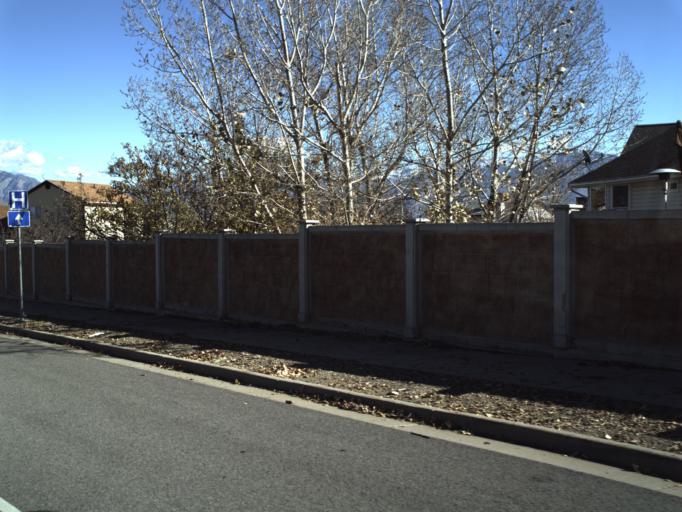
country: US
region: Utah
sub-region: Salt Lake County
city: Oquirrh
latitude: 40.5978
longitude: -112.0151
